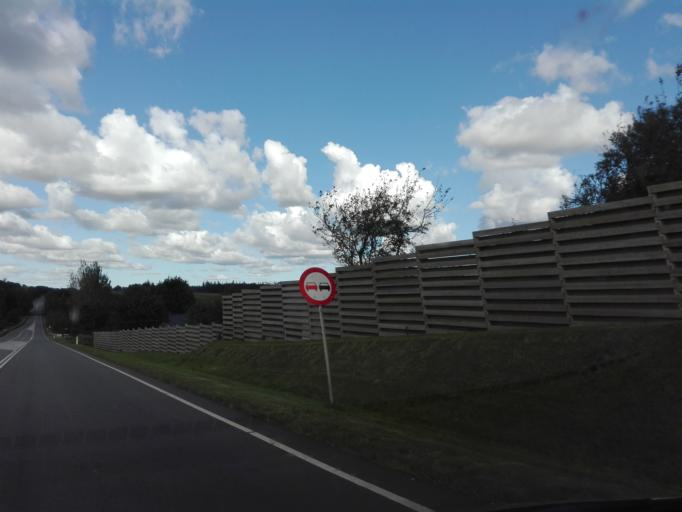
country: DK
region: North Denmark
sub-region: Mariagerfjord Kommune
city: Hobro
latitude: 56.5871
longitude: 9.8083
